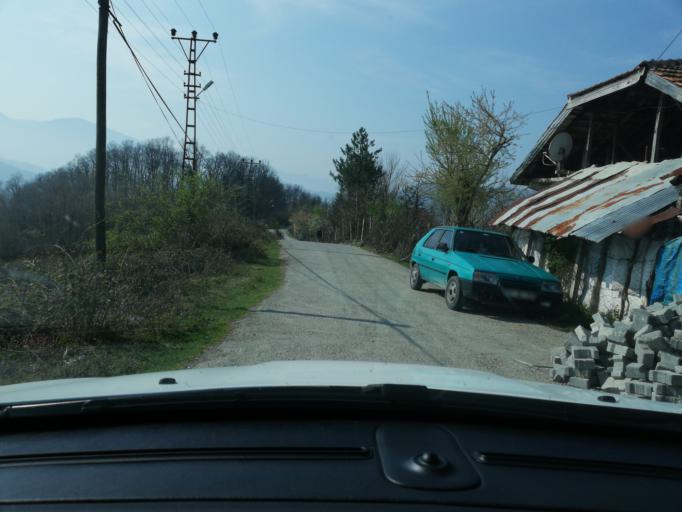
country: TR
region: Karabuk
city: Yenice
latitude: 41.2723
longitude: 32.3544
